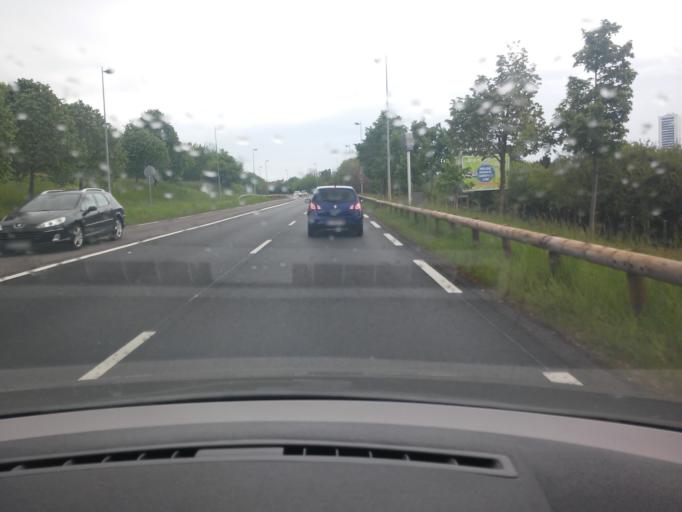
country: FR
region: Lorraine
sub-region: Departement de Meurthe-et-Moselle
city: Laxou
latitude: 48.6826
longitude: 6.1402
